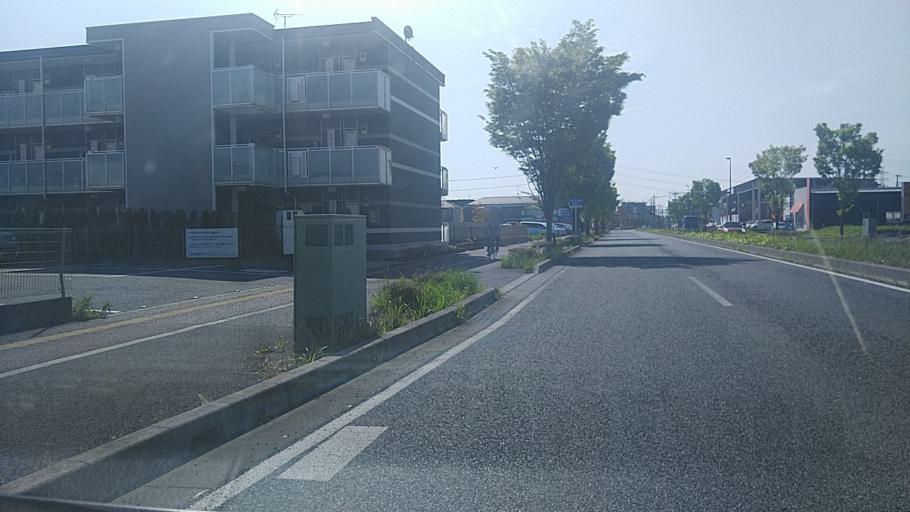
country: JP
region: Saitama
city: Koshigaya
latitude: 35.8868
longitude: 139.7374
